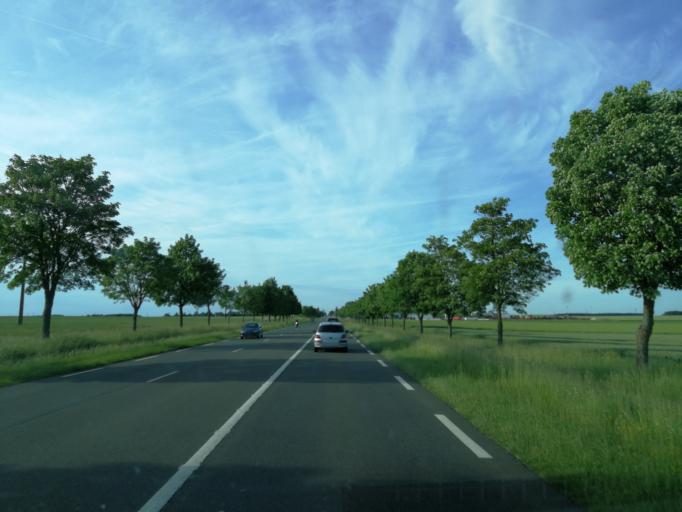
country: FR
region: Centre
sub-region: Departement d'Eure-et-Loir
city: Bonneval
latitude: 48.2468
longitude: 1.4102
